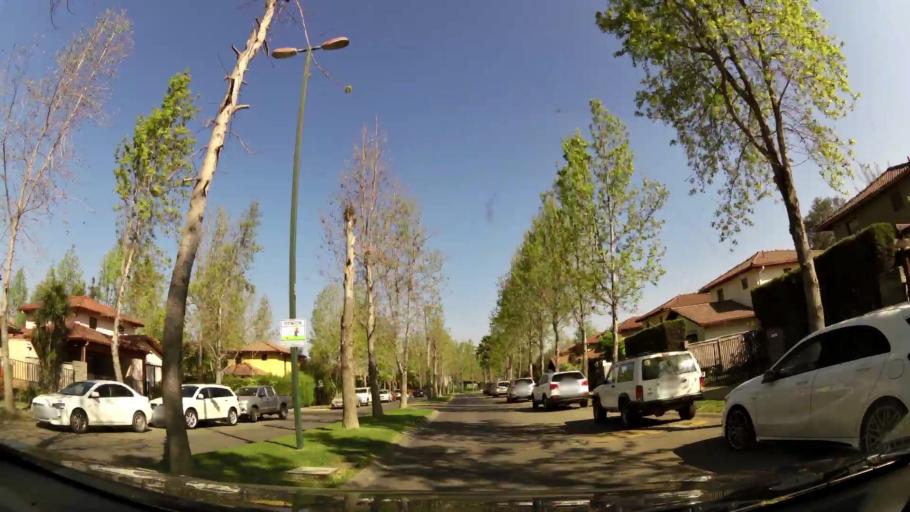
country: CL
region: Santiago Metropolitan
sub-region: Provincia de Chacabuco
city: Chicureo Abajo
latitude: -33.3587
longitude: -70.6778
